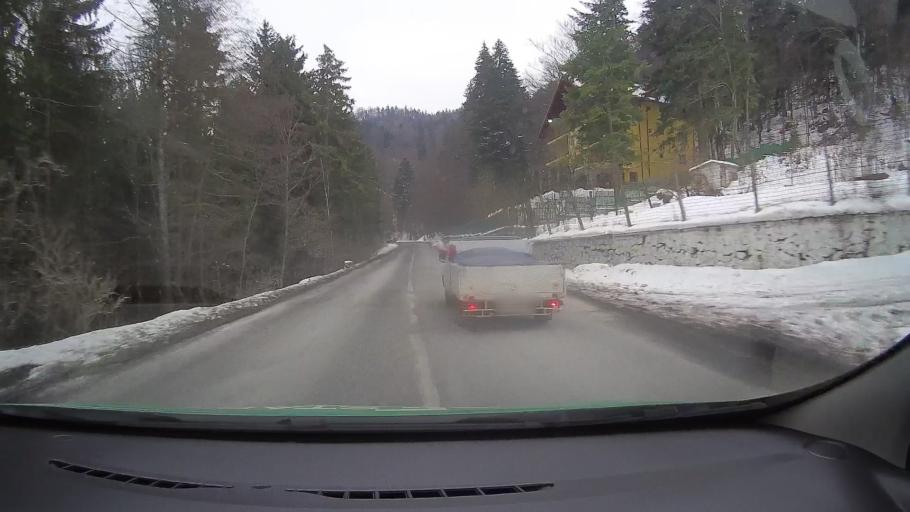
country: RO
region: Brasov
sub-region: Oras Predeal
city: Predeal
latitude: 45.5167
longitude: 25.5032
